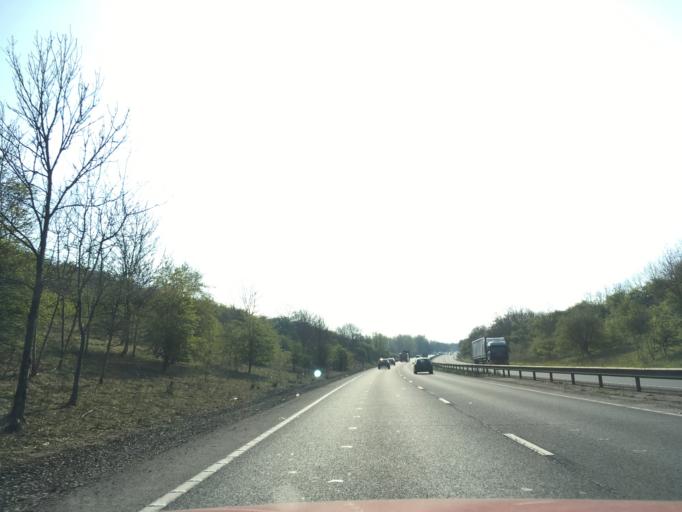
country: GB
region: England
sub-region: Milton Keynes
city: Stony Stratford
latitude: 52.0656
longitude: -0.8578
